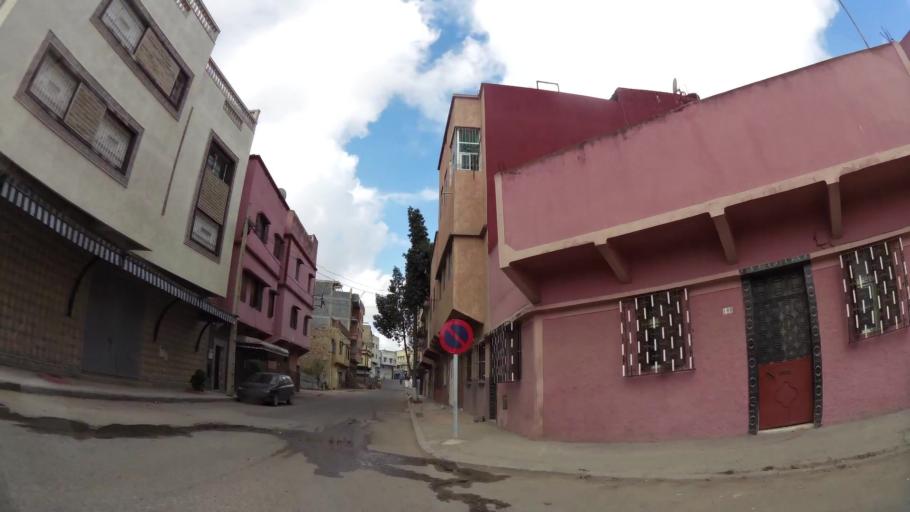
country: MA
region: Gharb-Chrarda-Beni Hssen
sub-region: Kenitra Province
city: Kenitra
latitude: 34.2656
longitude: -6.5667
